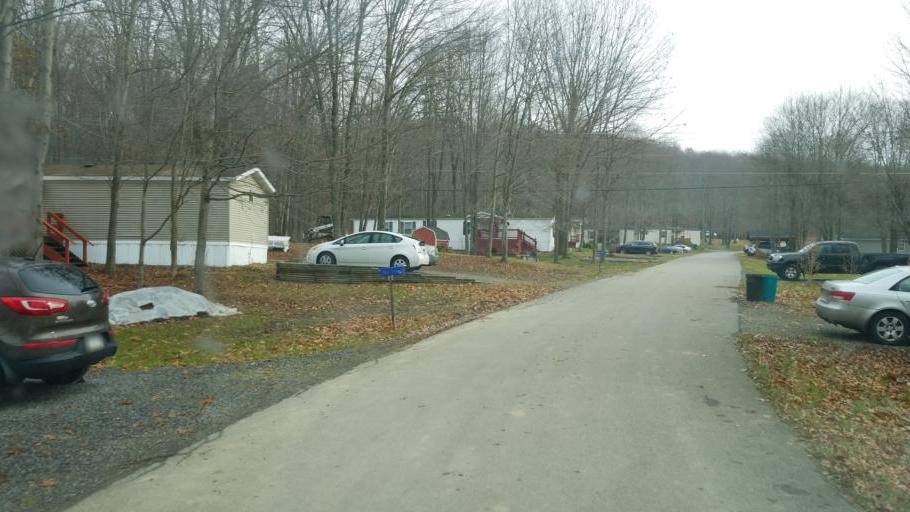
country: US
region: Pennsylvania
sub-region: Crawford County
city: Meadville
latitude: 41.5628
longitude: -80.1889
